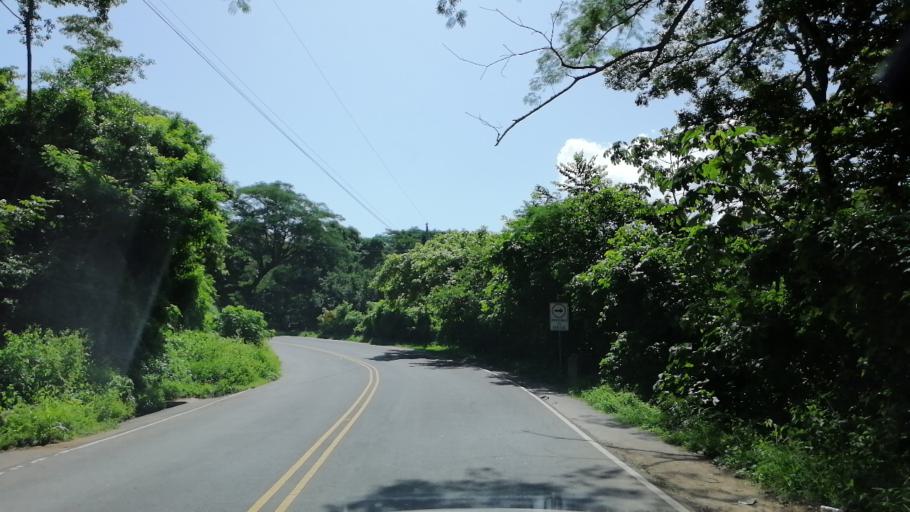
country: SV
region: Cabanas
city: Victoria
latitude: 13.9516
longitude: -88.7360
